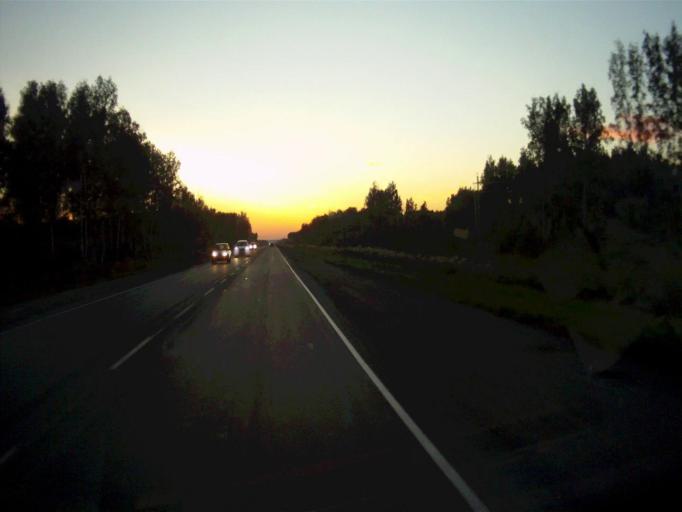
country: RU
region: Chelyabinsk
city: Poletayevo
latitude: 55.2103
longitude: 61.0827
